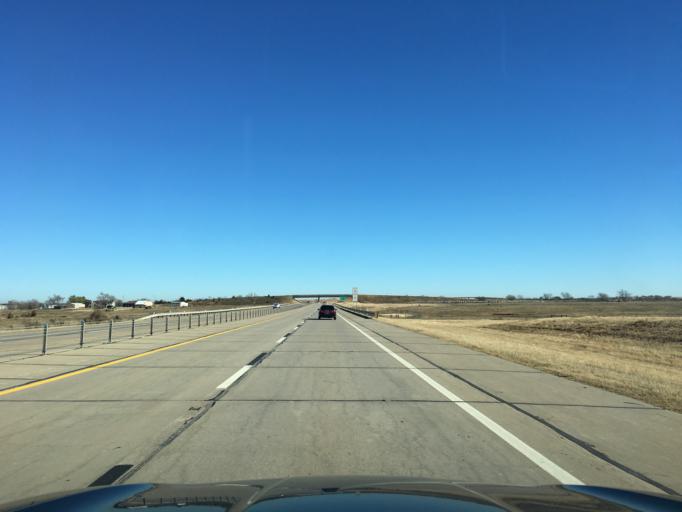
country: US
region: Oklahoma
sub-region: Noble County
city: Perry
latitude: 36.4003
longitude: -97.2706
